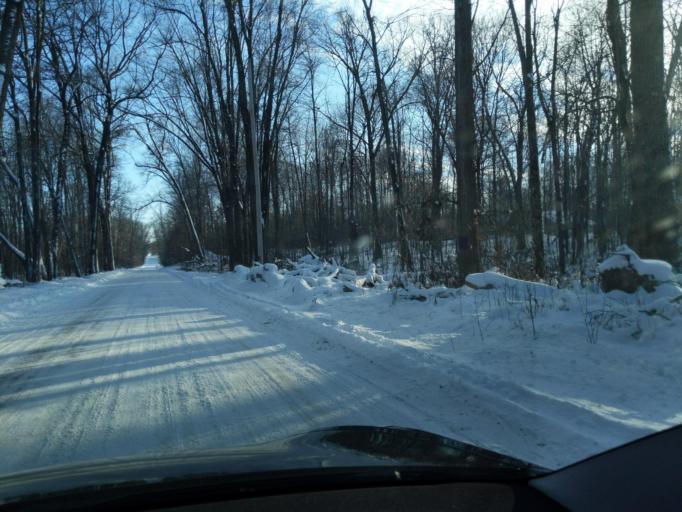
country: US
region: Michigan
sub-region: Ingham County
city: Stockbridge
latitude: 42.4651
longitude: -84.1191
